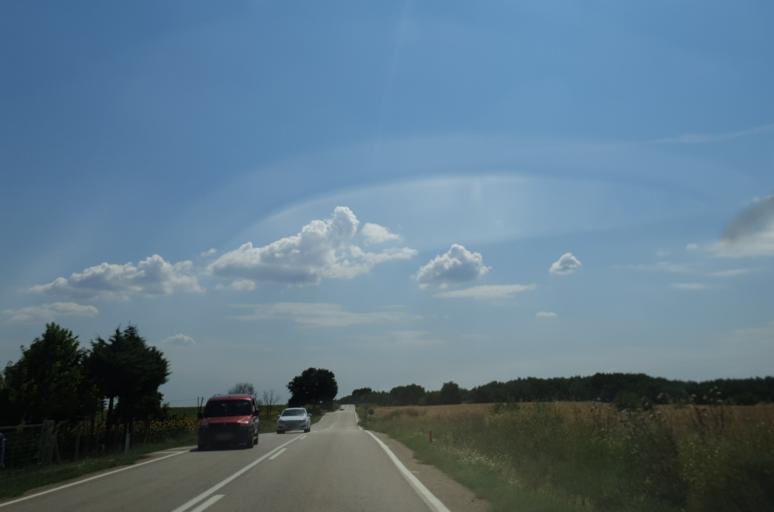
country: TR
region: Kirklareli
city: Vize
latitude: 41.4792
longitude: 27.6803
